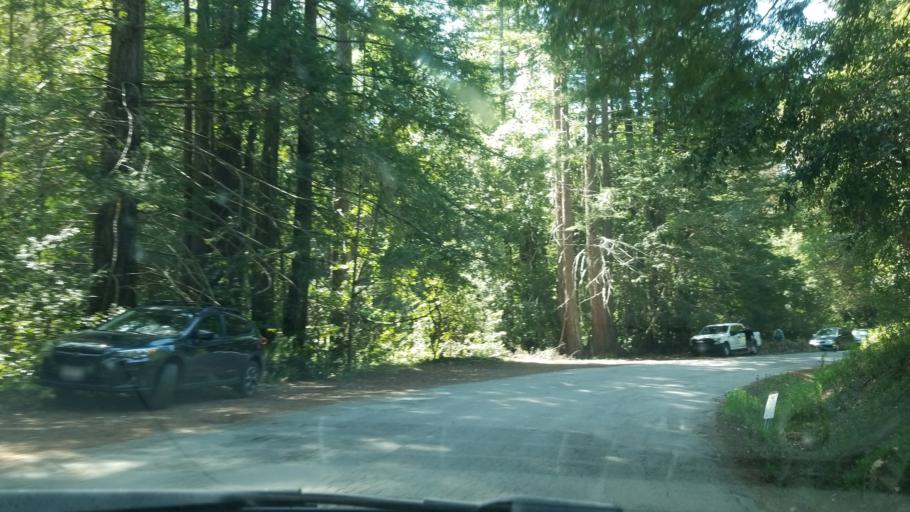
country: US
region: California
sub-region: Santa Cruz County
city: Day Valley
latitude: 37.0792
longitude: -121.8473
